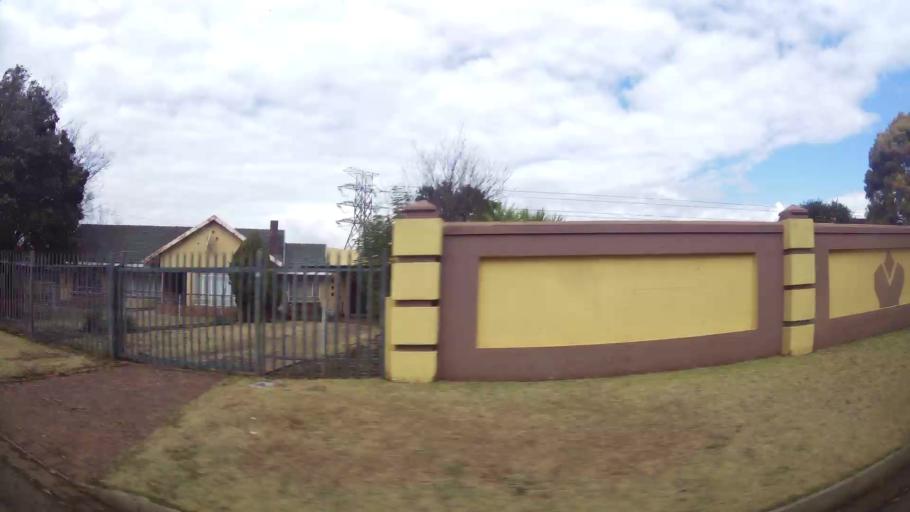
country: ZA
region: Gauteng
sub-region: Sedibeng District Municipality
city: Vereeniging
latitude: -26.6456
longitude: 27.9742
